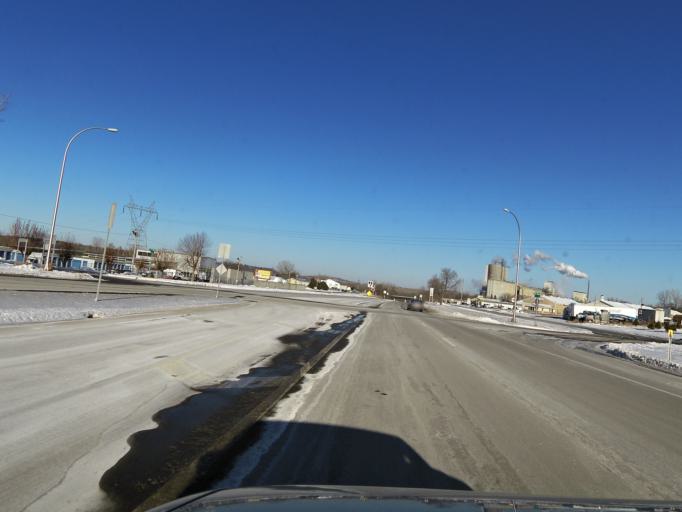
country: US
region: Minnesota
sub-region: Scott County
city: Shakopee
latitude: 44.7911
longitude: -93.5498
